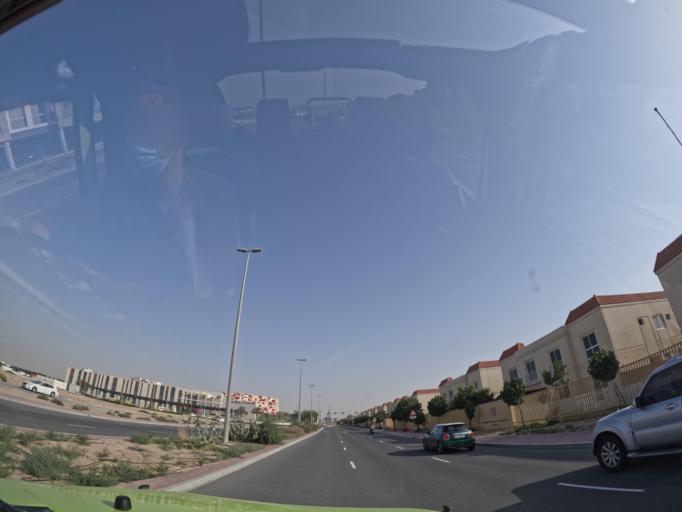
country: AE
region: Dubai
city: Dubai
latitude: 25.1270
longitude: 55.3557
